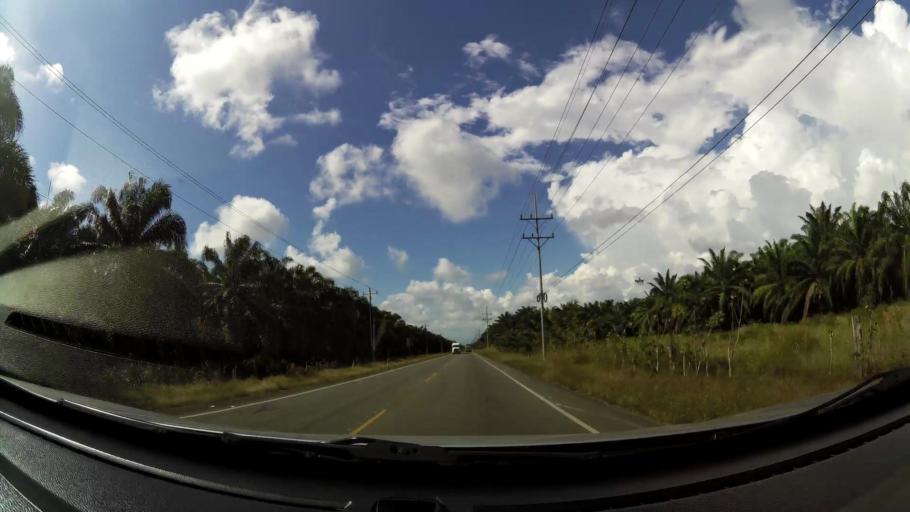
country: CR
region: Puntarenas
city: Quepos
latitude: 9.4706
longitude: -84.1904
